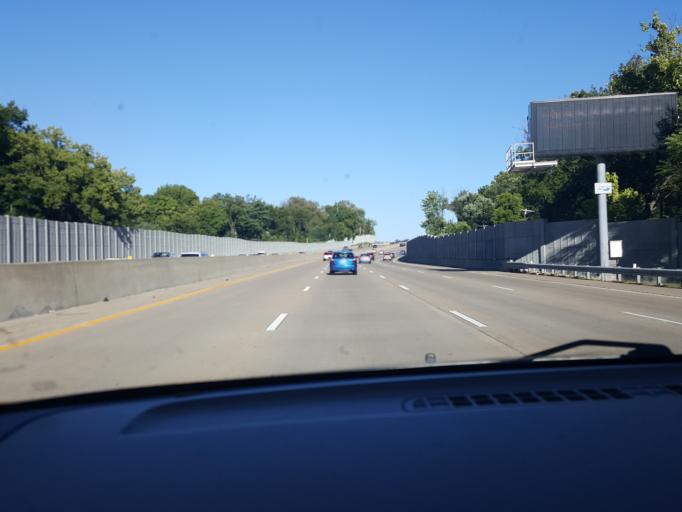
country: US
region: Missouri
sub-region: Saint Louis County
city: Ladue
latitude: 38.6311
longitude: -90.3729
